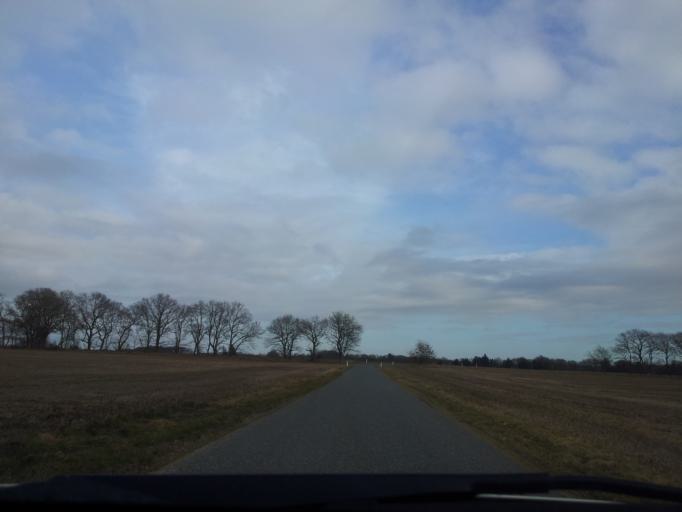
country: DK
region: South Denmark
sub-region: Vejen Kommune
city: Brorup
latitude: 55.4519
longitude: 9.0402
